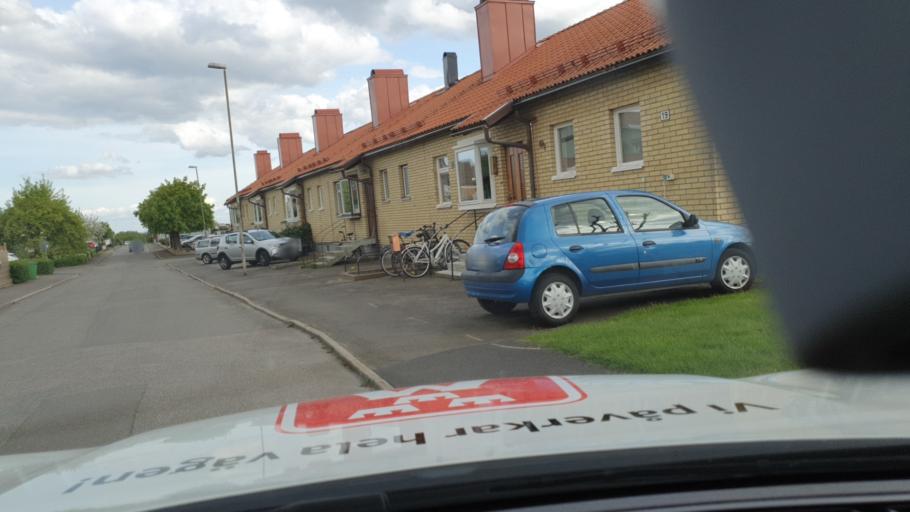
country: SE
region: Vaestra Goetaland
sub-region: Skovde Kommun
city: Skoevde
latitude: 58.4025
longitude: 13.8585
